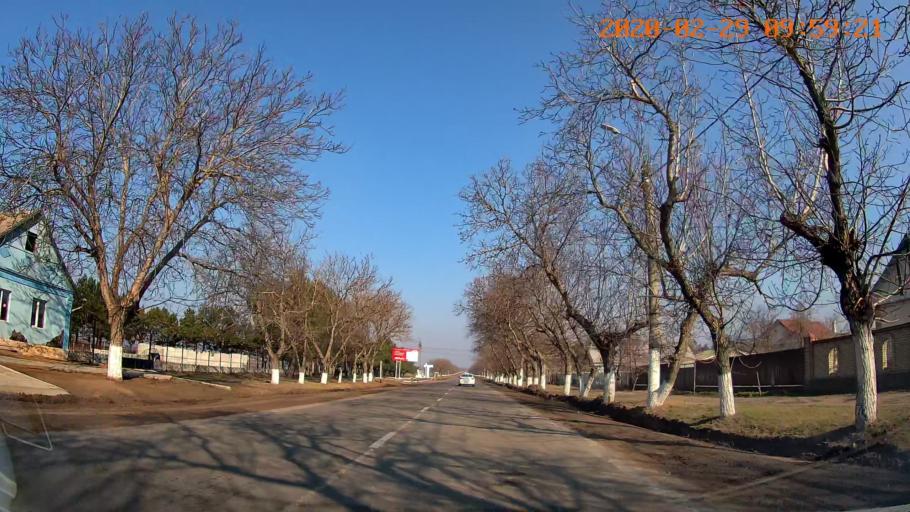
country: MD
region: Telenesti
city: Slobozia
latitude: 46.7560
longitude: 29.6886
